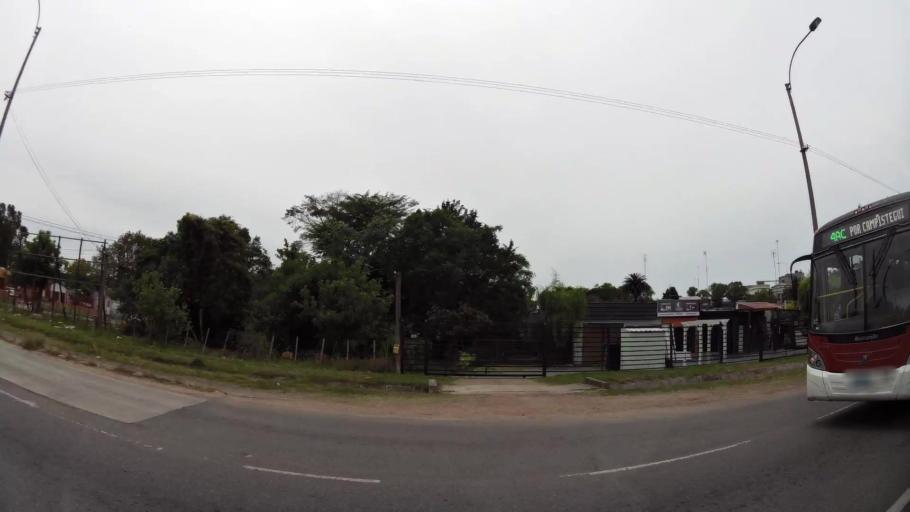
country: UY
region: Canelones
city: La Paz
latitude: -34.7691
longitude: -56.2275
